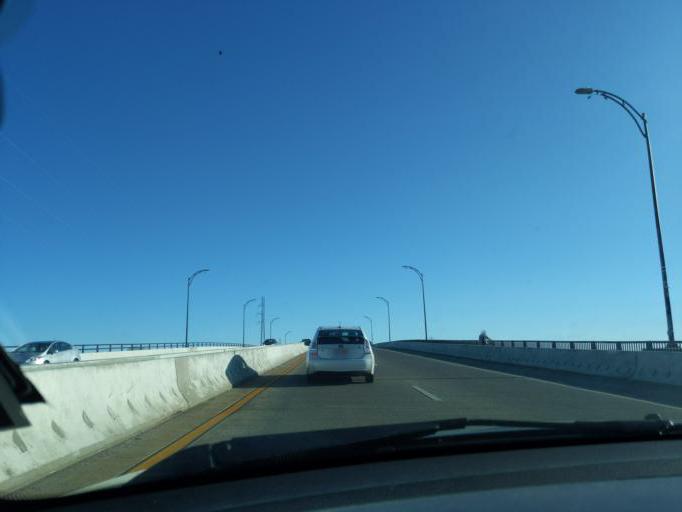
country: US
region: Massachusetts
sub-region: Essex County
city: Salem
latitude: 42.5375
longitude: -70.8880
